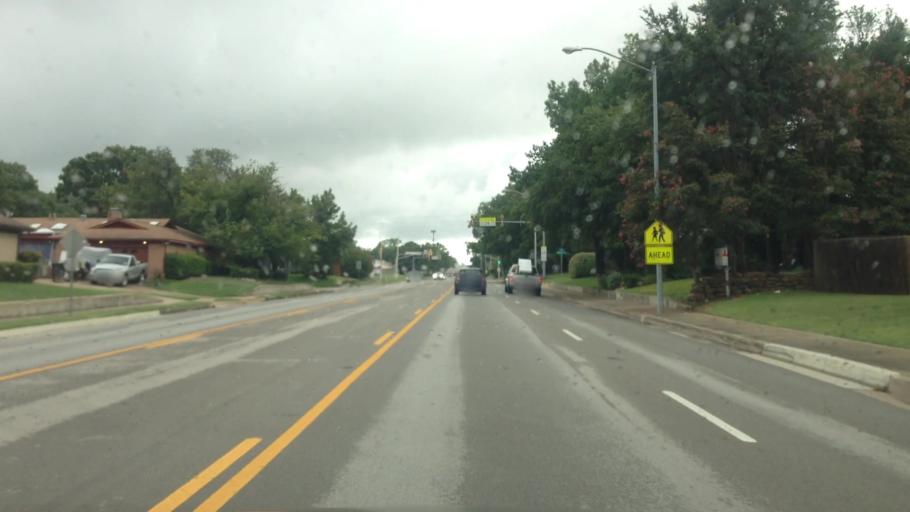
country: US
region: Texas
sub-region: Tarrant County
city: Edgecliff Village
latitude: 32.6567
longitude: -97.3959
